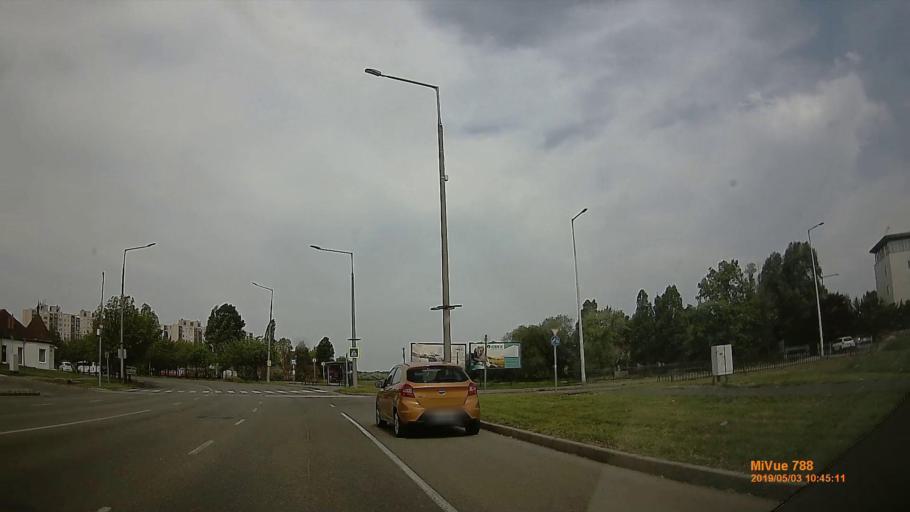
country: HU
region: Jasz-Nagykun-Szolnok
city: Szolnok
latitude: 47.1935
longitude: 20.1904
